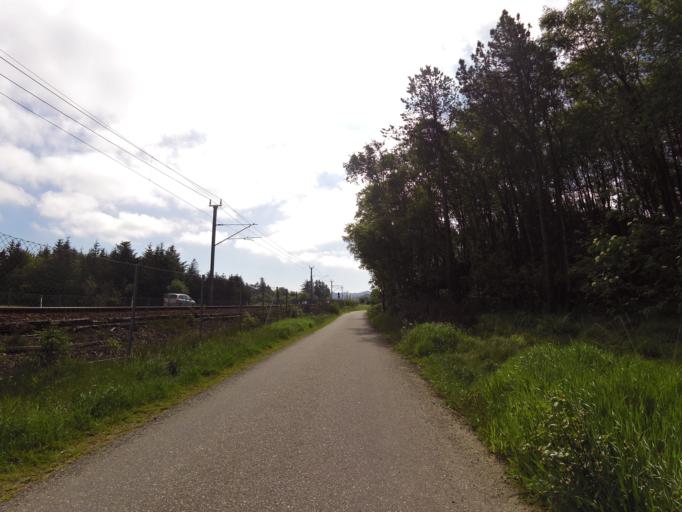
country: NO
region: Rogaland
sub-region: Ha
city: Vigrestad
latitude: 58.5237
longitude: 5.7932
